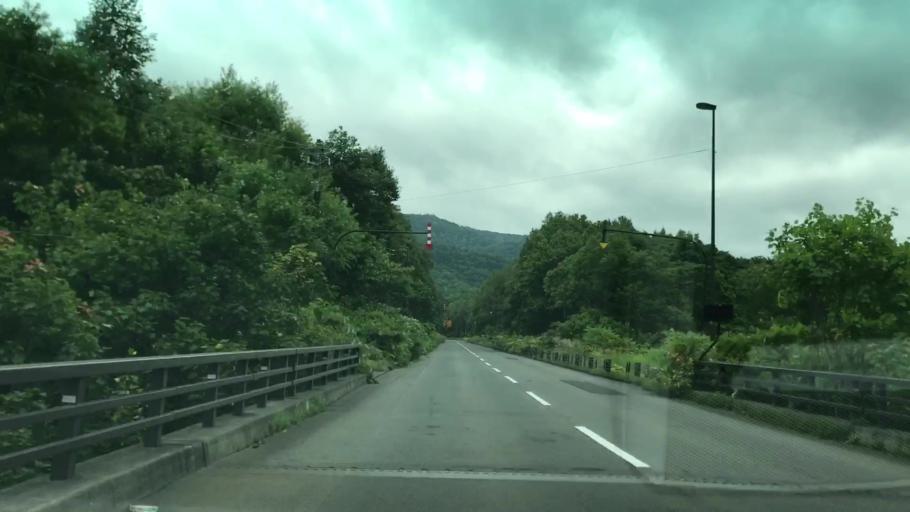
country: JP
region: Hokkaido
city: Yoichi
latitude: 43.0093
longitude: 140.8721
